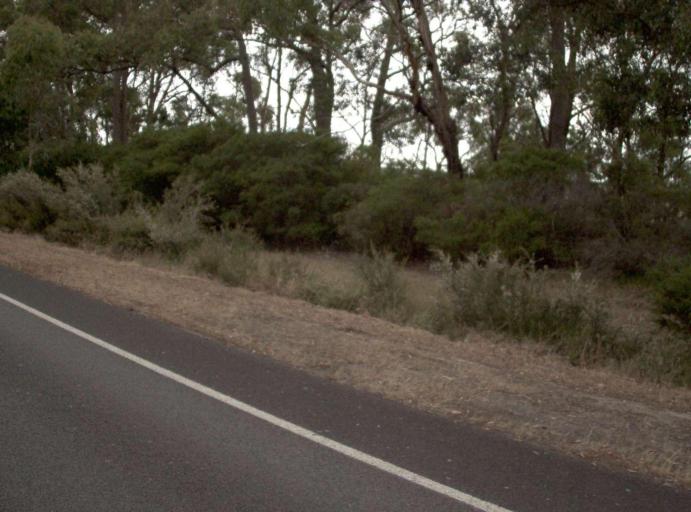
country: AU
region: Victoria
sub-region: Wellington
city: Sale
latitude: -38.4846
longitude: 146.9154
